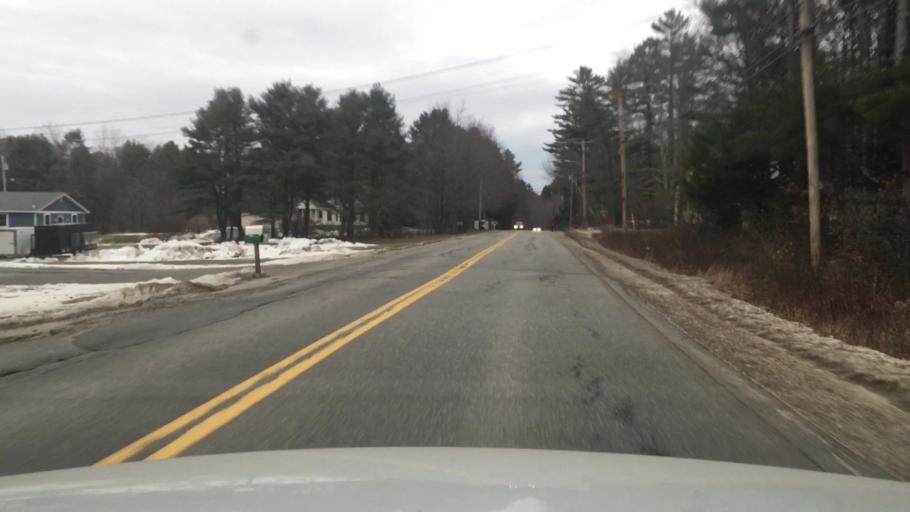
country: US
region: Maine
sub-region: Sagadahoc County
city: Topsham
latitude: 43.8989
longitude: -70.0006
